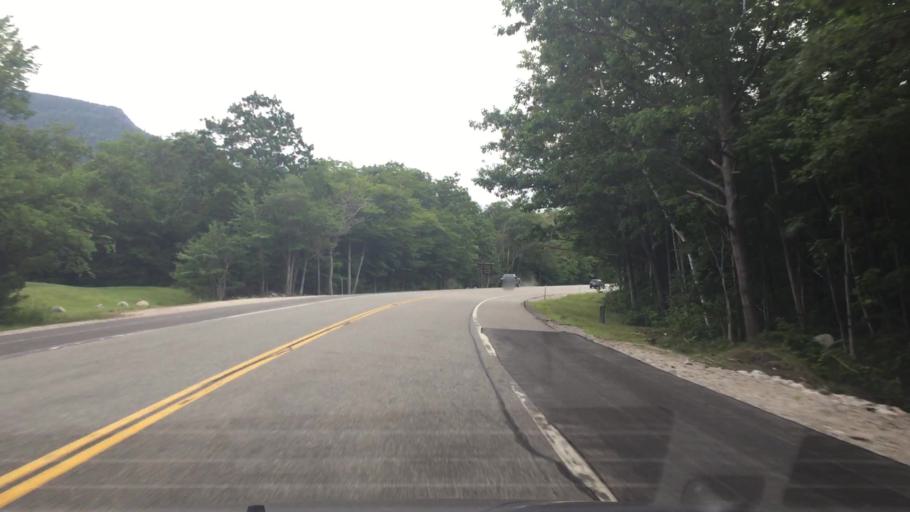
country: US
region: New Hampshire
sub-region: Carroll County
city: North Conway
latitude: 44.1565
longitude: -71.3638
